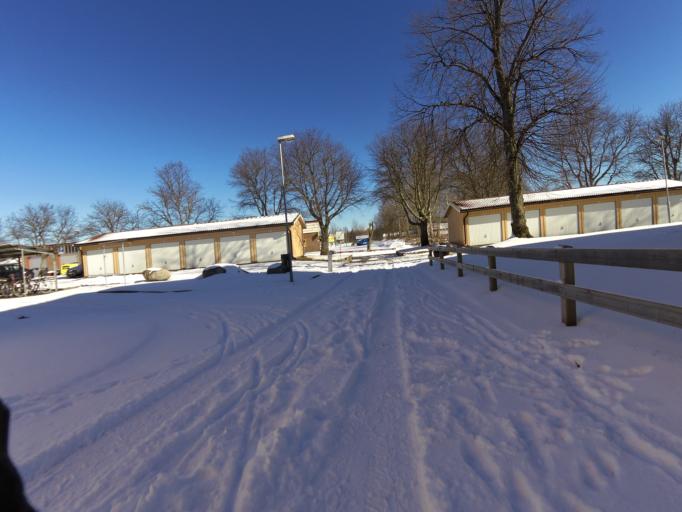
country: SE
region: Gaevleborg
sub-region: Gavle Kommun
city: Gavle
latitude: 60.6753
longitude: 17.1795
